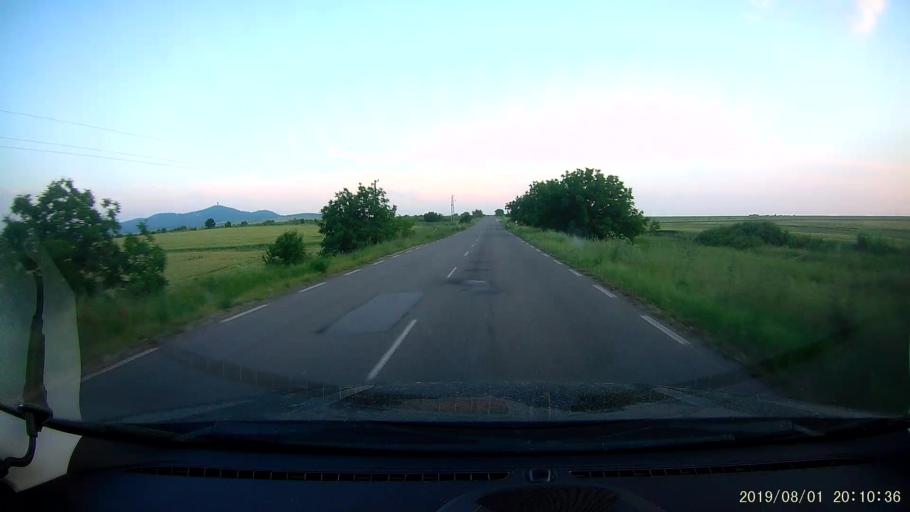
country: BG
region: Yambol
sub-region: Obshtina Yambol
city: Yambol
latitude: 42.4783
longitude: 26.6008
